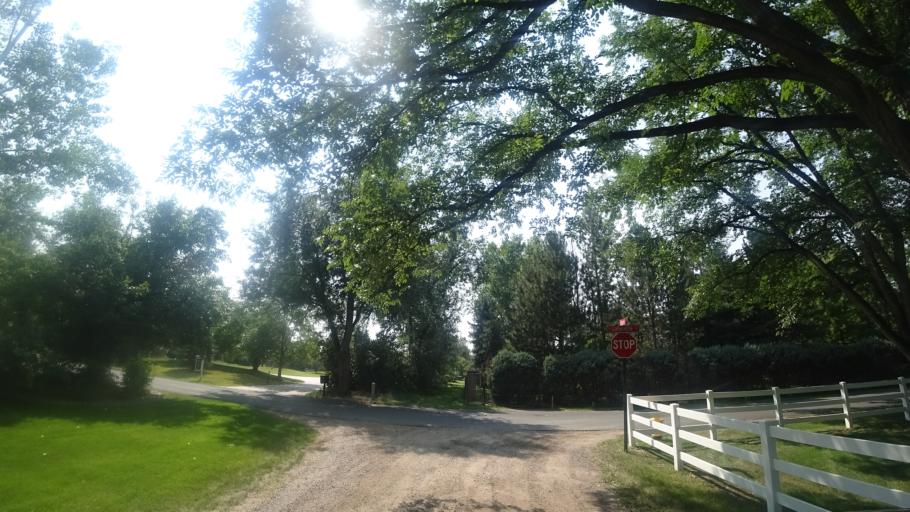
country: US
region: Colorado
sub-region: Arapahoe County
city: Cherry Hills Village
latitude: 39.6368
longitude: -104.9713
